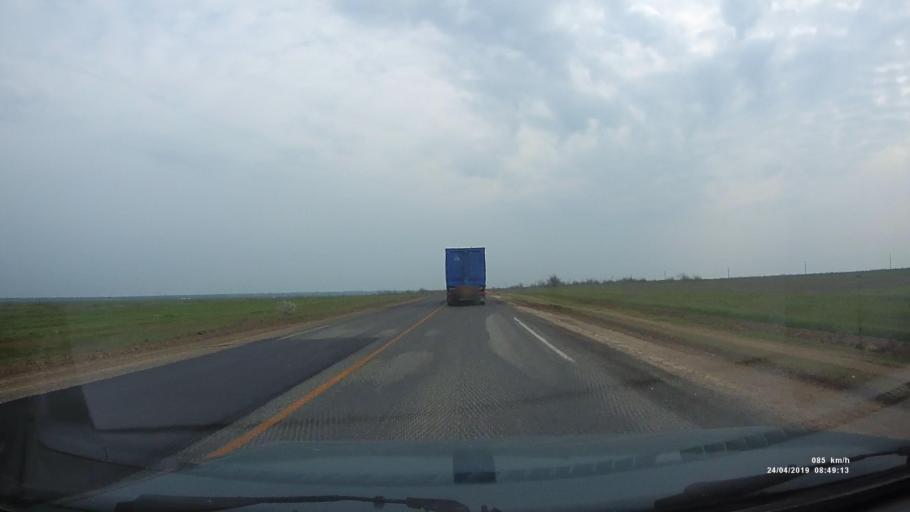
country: RU
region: Kalmykiya
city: Arshan'
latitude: 46.2557
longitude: 44.1210
